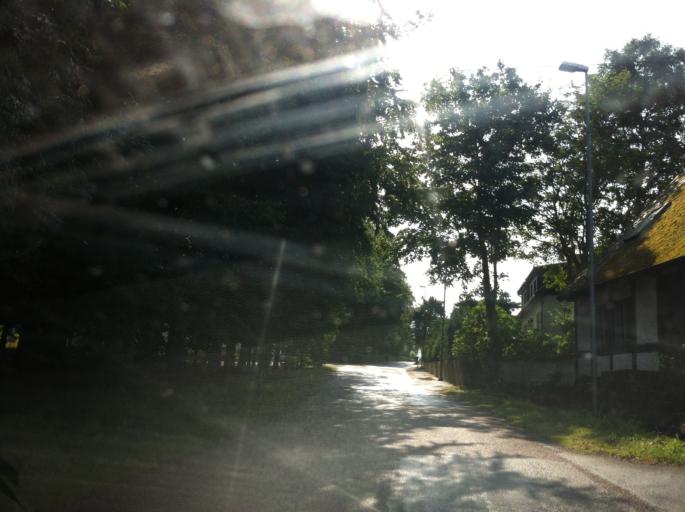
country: SE
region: Skane
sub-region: Helsingborg
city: Glumslov
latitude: 55.9306
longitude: 12.8741
